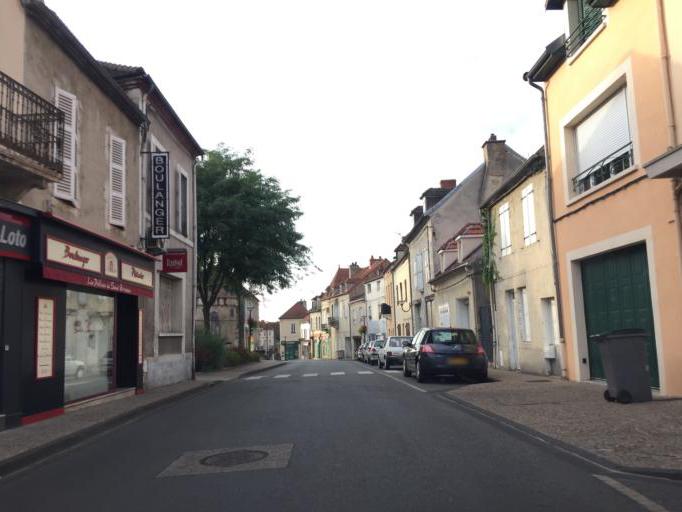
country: FR
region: Auvergne
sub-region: Departement de l'Allier
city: Saint-Germain-des-Fosses
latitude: 46.2031
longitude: 3.4332
